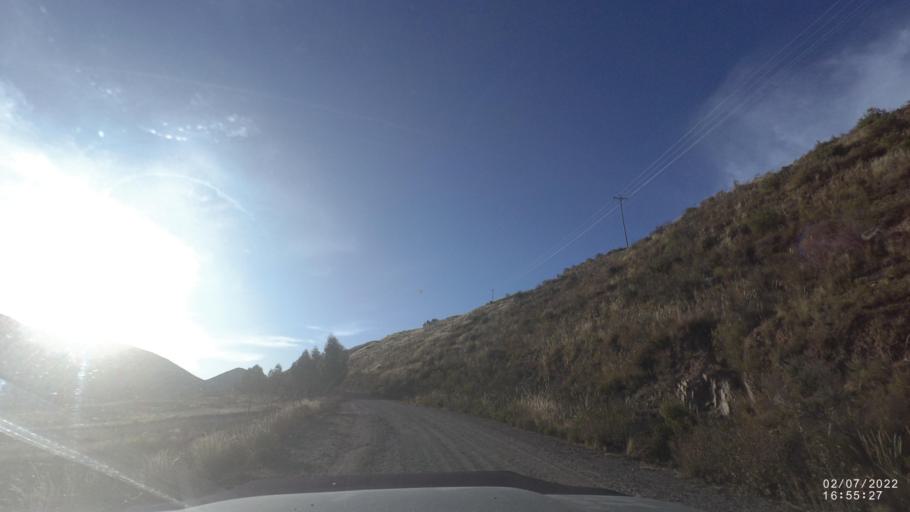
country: BO
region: Cochabamba
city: Irpa Irpa
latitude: -17.9602
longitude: -66.5409
